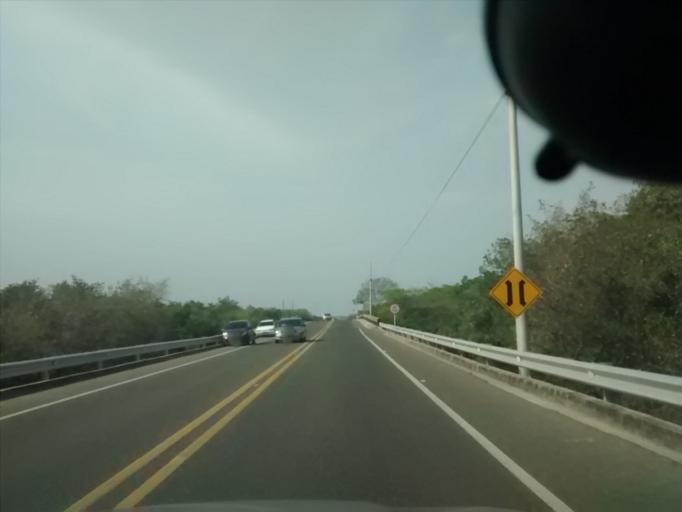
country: CO
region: Bolivar
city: Cartagena
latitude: 10.4906
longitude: -75.4826
